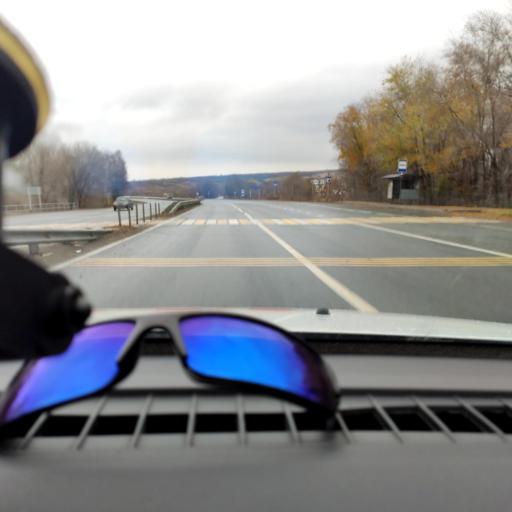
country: RU
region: Samara
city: Novokuybyshevsk
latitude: 53.0541
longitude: 50.0152
